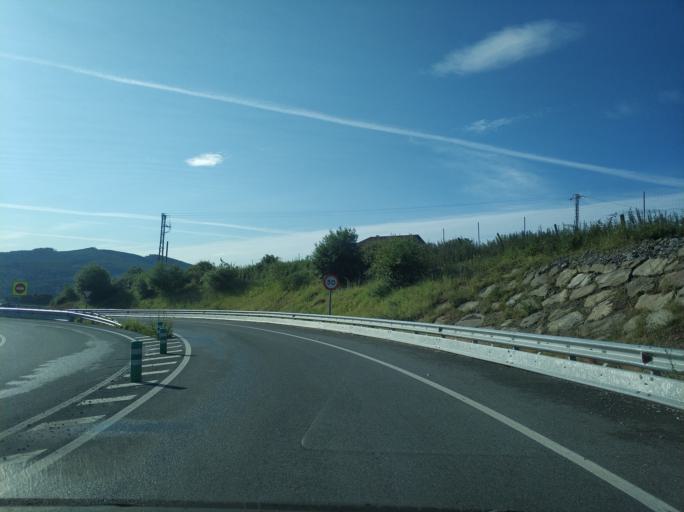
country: ES
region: Cantabria
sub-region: Provincia de Cantabria
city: Polanco
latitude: 43.3428
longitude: -3.9943
